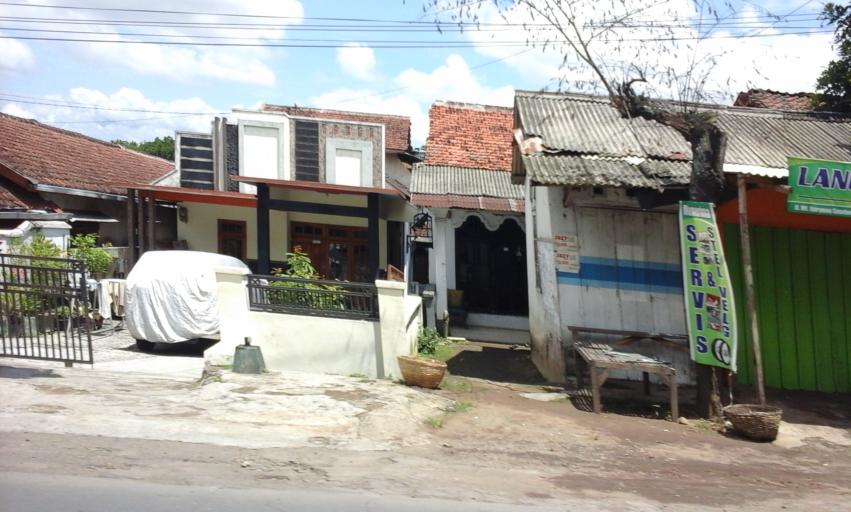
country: ID
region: East Java
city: Kloncing
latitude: -8.1865
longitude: 113.7311
